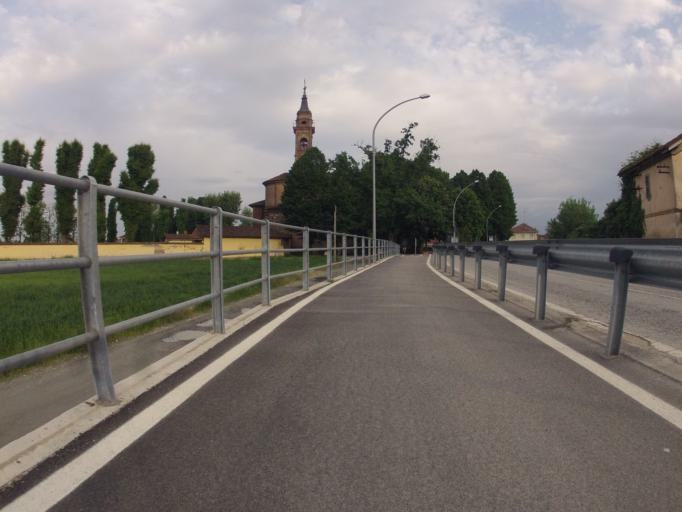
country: IT
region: Piedmont
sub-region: Provincia di Cuneo
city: Moretta
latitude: 44.7680
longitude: 7.5296
